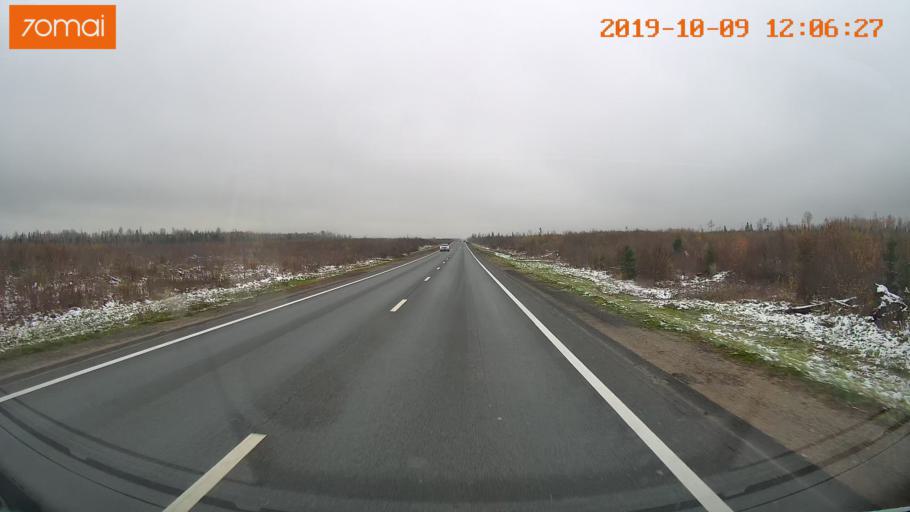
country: RU
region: Jaroslavl
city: Prechistoye
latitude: 58.6142
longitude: 40.3353
